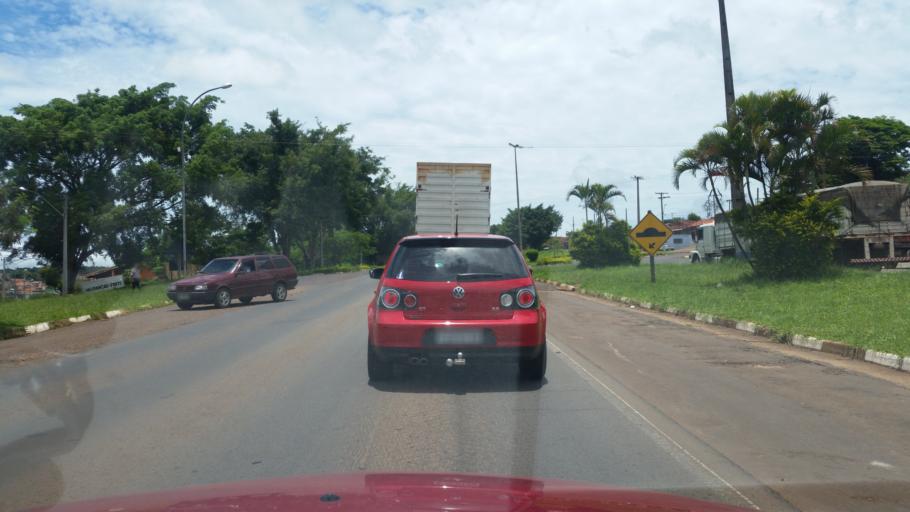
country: BR
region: Sao Paulo
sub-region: Itai
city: Itai
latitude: -23.4142
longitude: -49.0931
